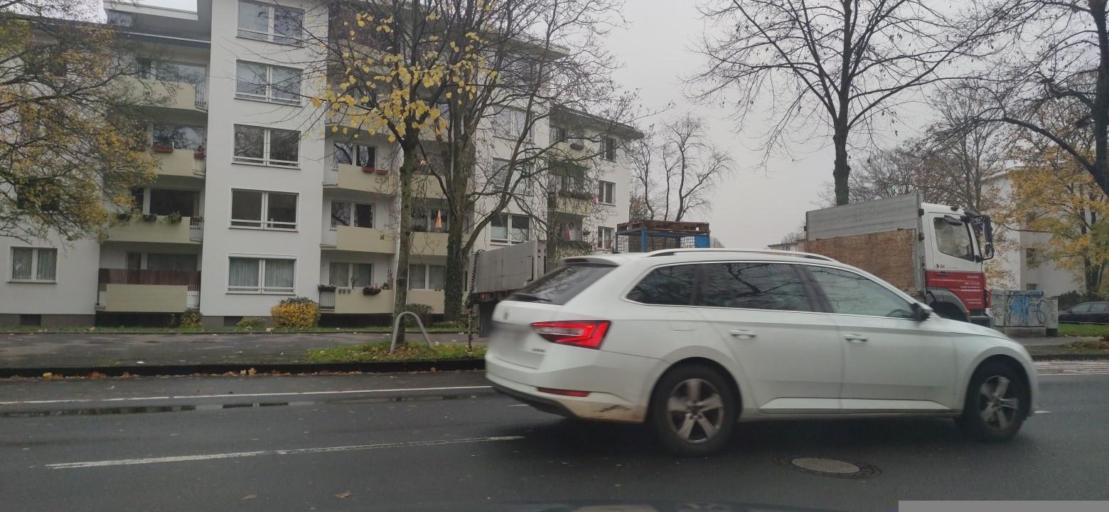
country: DE
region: North Rhine-Westphalia
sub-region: Regierungsbezirk Dusseldorf
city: Erkrath
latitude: 51.1980
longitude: 6.8464
